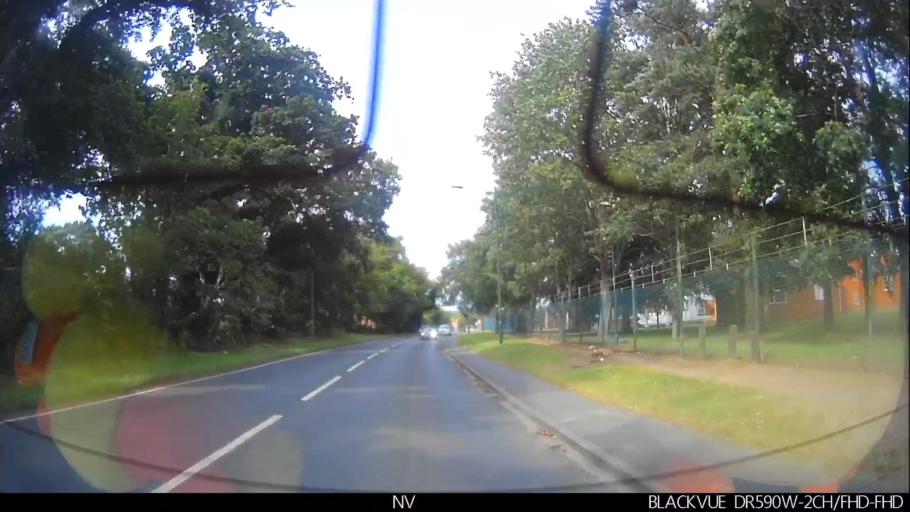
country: GB
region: England
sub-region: North Yorkshire
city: Strensall
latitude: 54.0259
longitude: -1.0424
